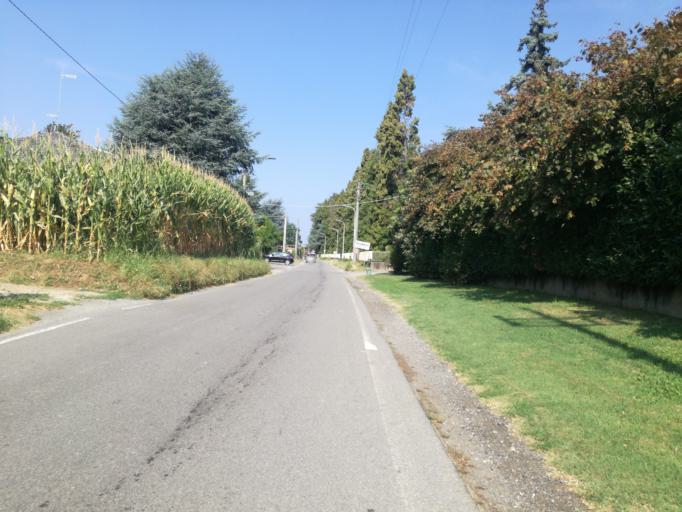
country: IT
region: Lombardy
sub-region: Provincia di Monza e Brianza
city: Cornate d'Adda
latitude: 45.6286
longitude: 9.4779
